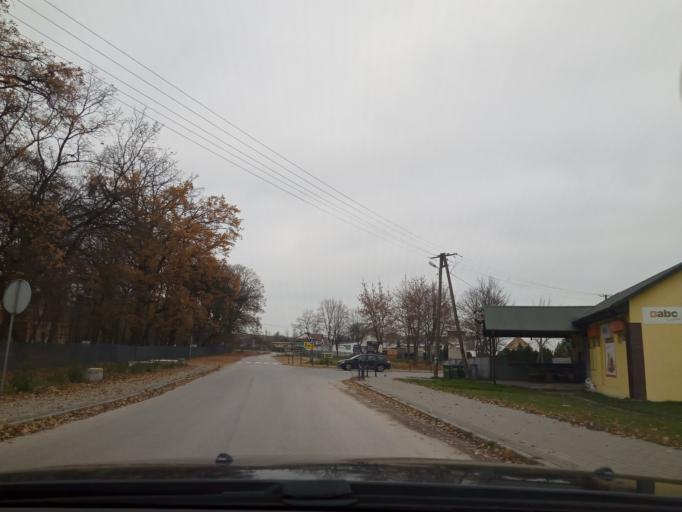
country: PL
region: Swietokrzyskie
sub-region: Powiat jedrzejowski
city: Imielno
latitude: 50.6038
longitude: 20.4911
